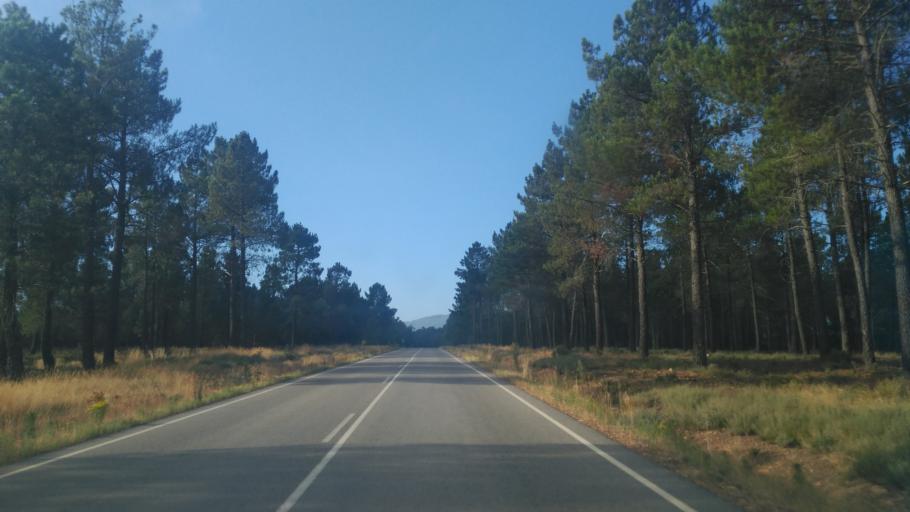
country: ES
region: Castille and Leon
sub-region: Provincia de Salamanca
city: Nava de Francia
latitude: 40.5316
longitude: -6.1377
